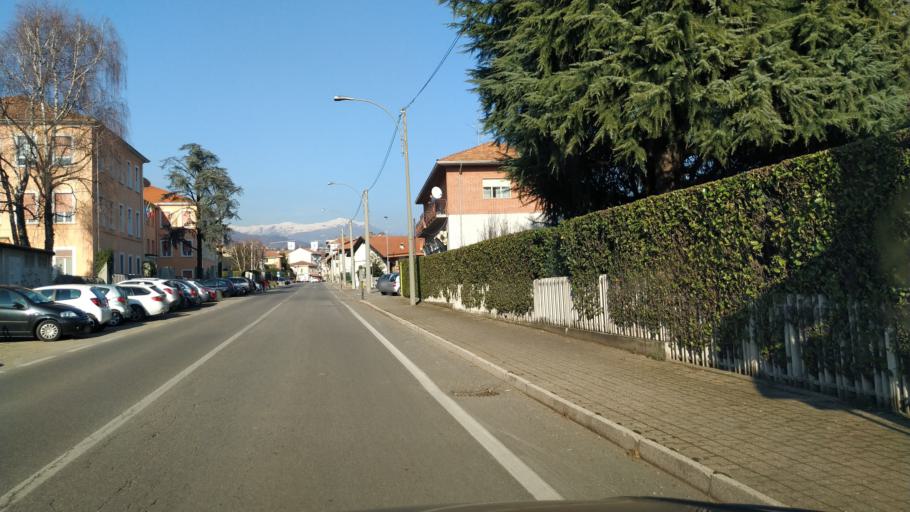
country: IT
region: Piedmont
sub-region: Provincia di Biella
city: Occhieppo Inferiore
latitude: 45.5478
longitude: 8.0146
